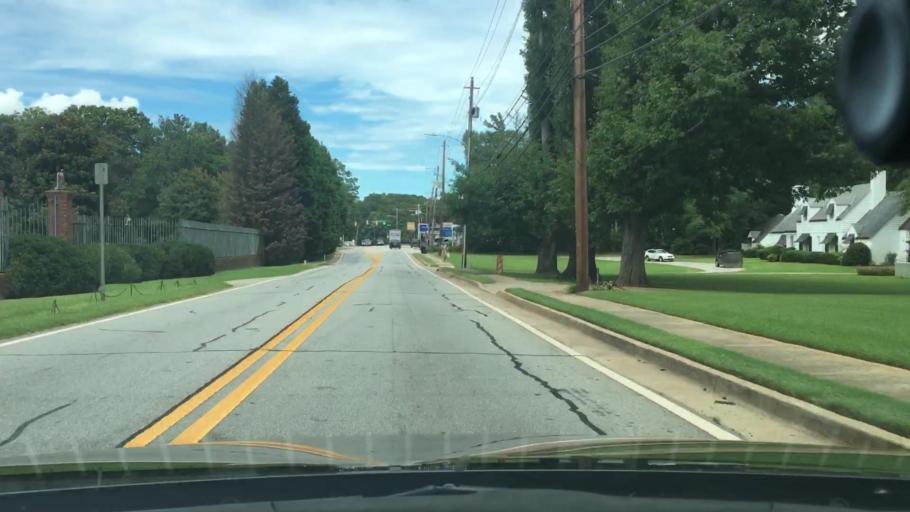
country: US
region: Georgia
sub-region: Coweta County
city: Newnan
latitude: 33.3910
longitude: -84.8011
